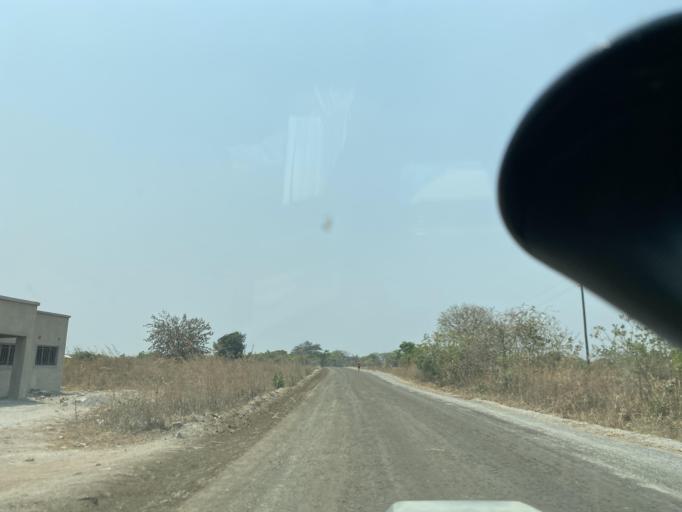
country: ZM
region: Lusaka
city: Lusaka
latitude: -15.5596
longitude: 28.4366
